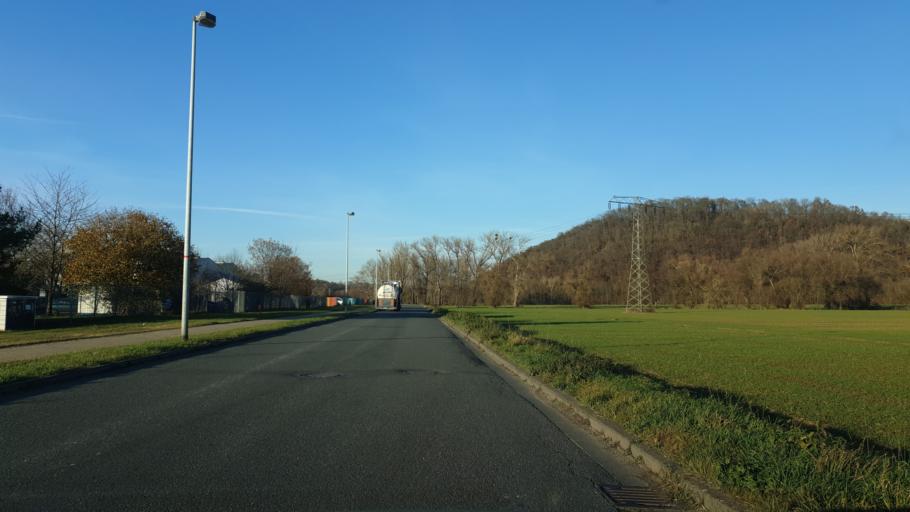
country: DE
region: Thuringia
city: Hartmannsdorf
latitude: 50.9659
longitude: 11.9886
